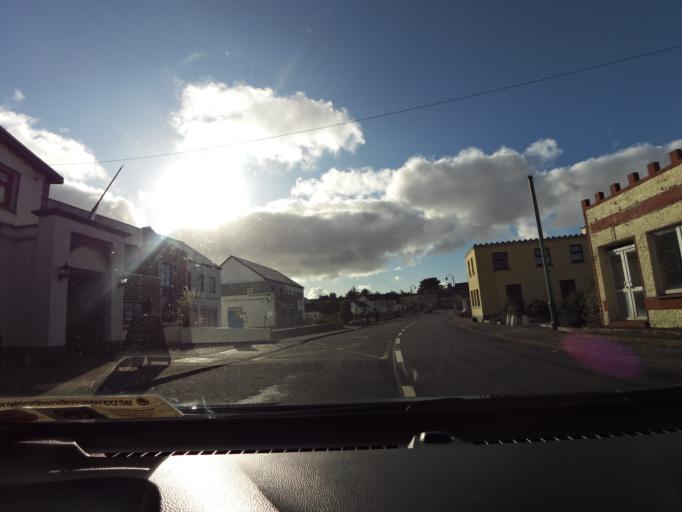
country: IE
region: Connaught
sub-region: Maigh Eo
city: Belmullet
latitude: 53.9307
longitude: -9.9253
